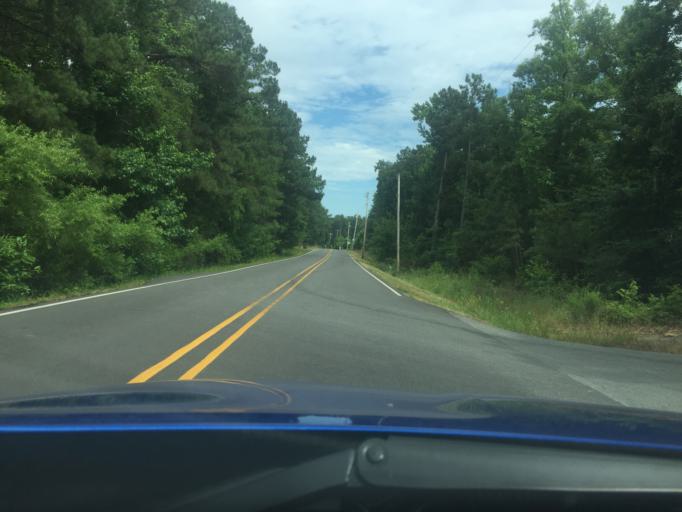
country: US
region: Arkansas
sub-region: Pulaski County
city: Maumelle
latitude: 34.8338
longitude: -92.4536
